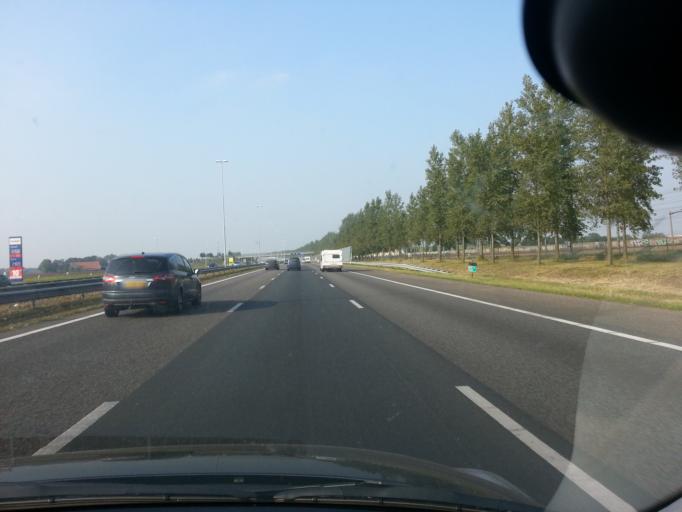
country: NL
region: North Brabant
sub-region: Gemeente Made en Drimmelen
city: Made
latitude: 51.6627
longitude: 4.6804
